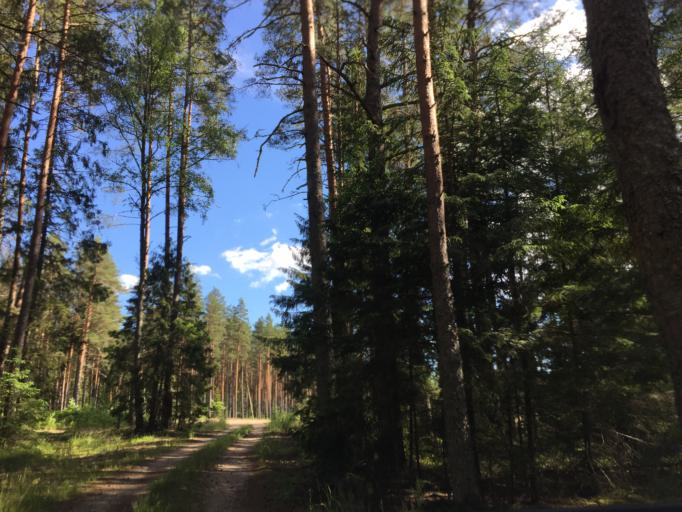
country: LV
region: Ventspils Rajons
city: Piltene
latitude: 57.0996
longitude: 21.8047
